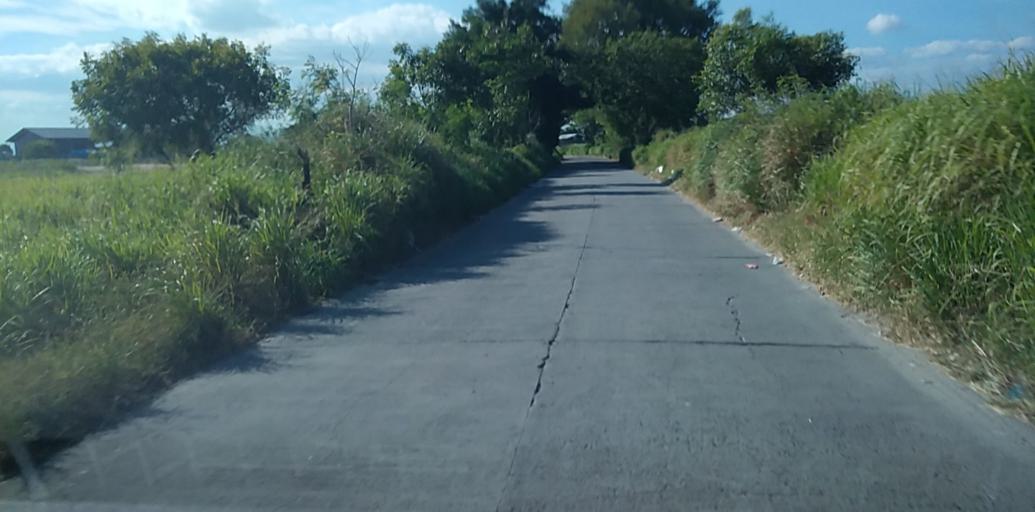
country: PH
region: Central Luzon
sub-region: Province of Pampanga
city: Acli
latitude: 15.1161
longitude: 120.6442
